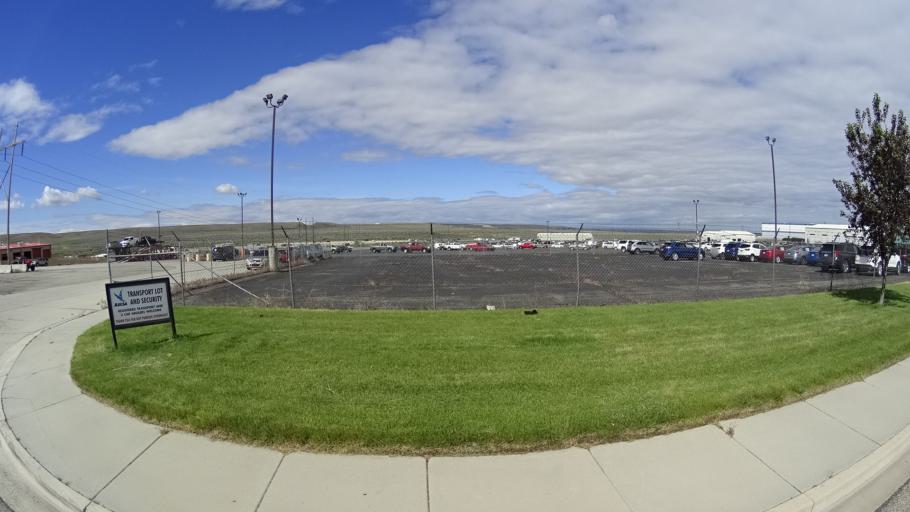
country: US
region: Idaho
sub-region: Ada County
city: Boise
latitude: 43.5351
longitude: -116.1607
